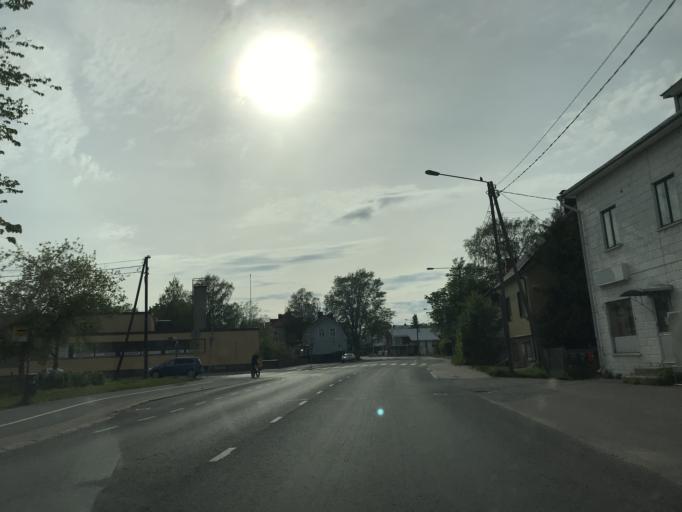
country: FI
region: Varsinais-Suomi
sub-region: Turku
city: Turku
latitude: 60.4556
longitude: 22.3069
